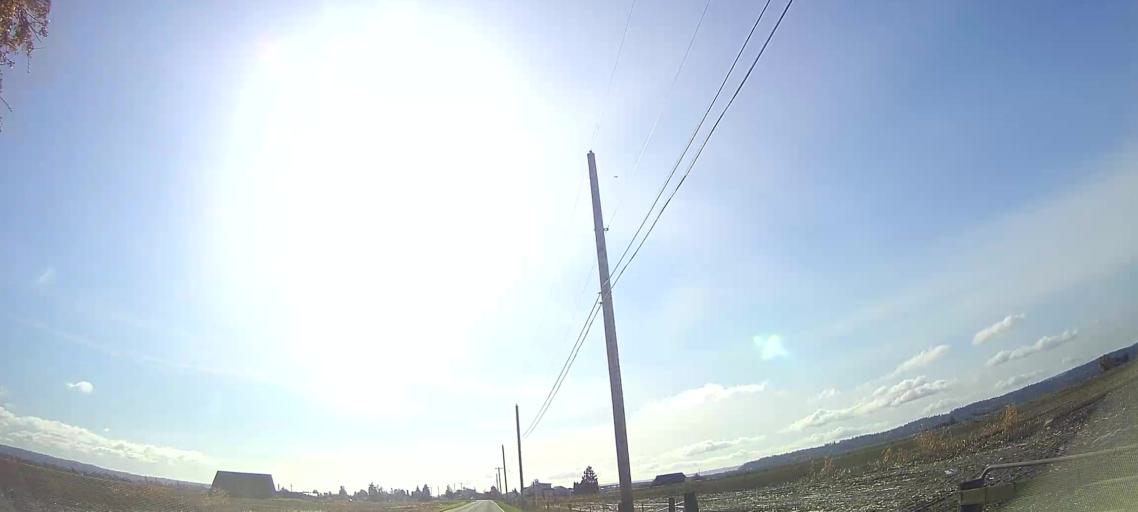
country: US
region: Washington
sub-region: Snohomish County
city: Stanwood
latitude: 48.2606
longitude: -122.3698
